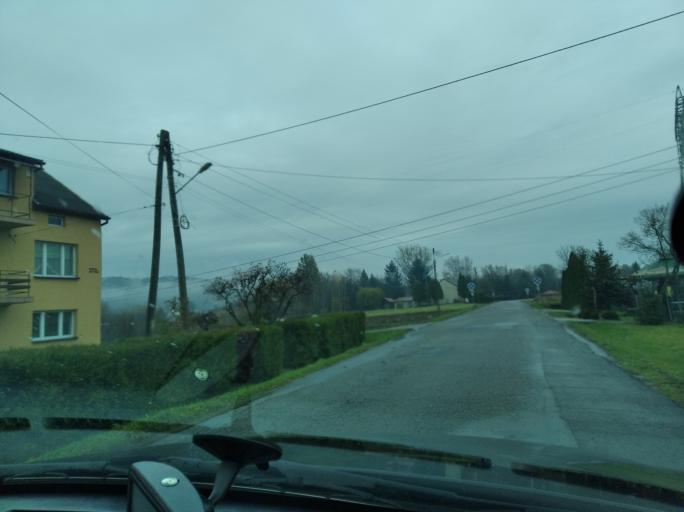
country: PL
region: Subcarpathian Voivodeship
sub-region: Powiat strzyzowski
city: Babica
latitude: 49.9269
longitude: 21.8684
